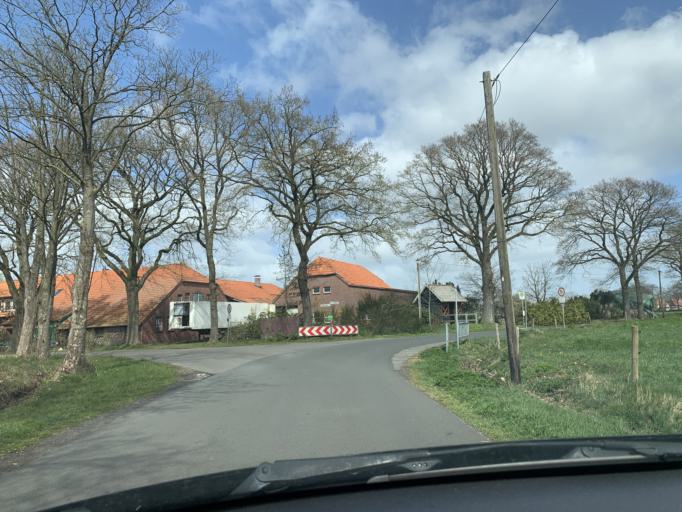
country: DE
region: Lower Saxony
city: Westerstede
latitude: 53.2990
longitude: 7.9448
